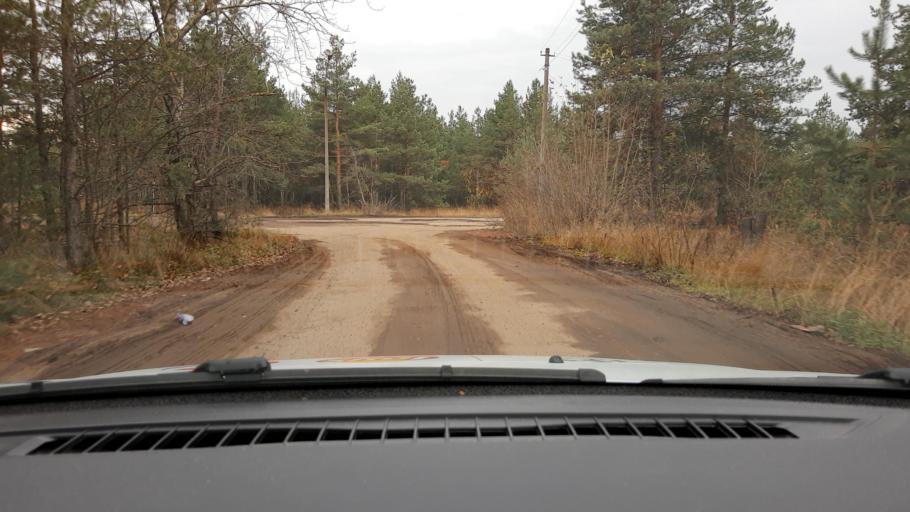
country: RU
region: Nizjnij Novgorod
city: Dzerzhinsk
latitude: 56.2776
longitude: 43.4774
